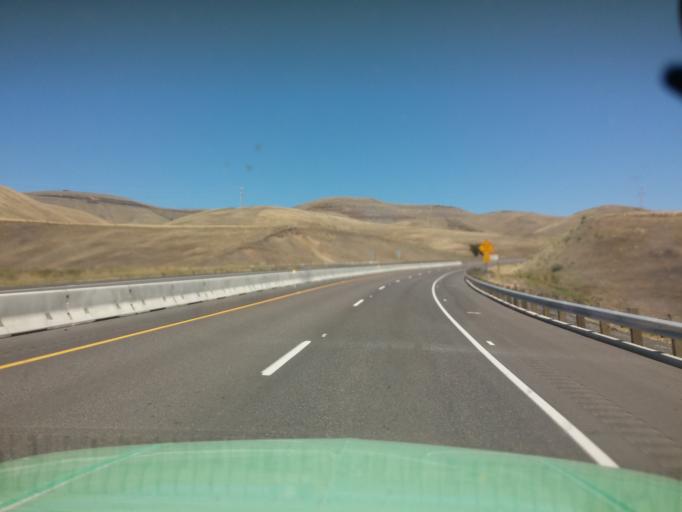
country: US
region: Idaho
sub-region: Nez Perce County
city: Lewiston
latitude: 46.4420
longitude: -116.9848
